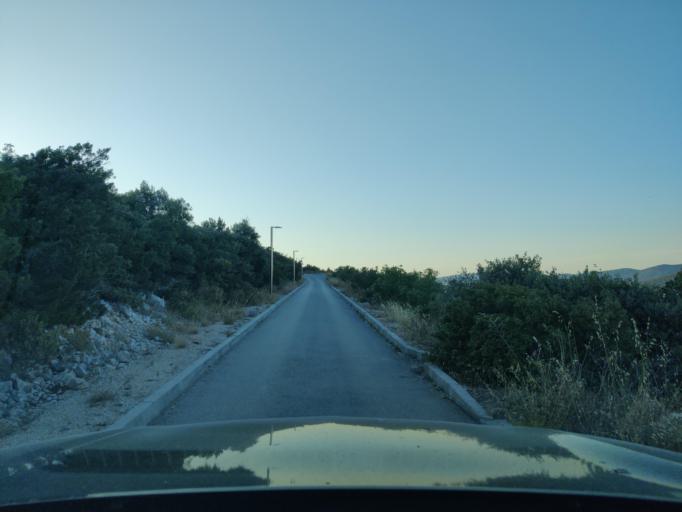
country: HR
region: Sibensko-Kniniska
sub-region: Grad Sibenik
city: Tisno
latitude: 43.8112
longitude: 15.6277
